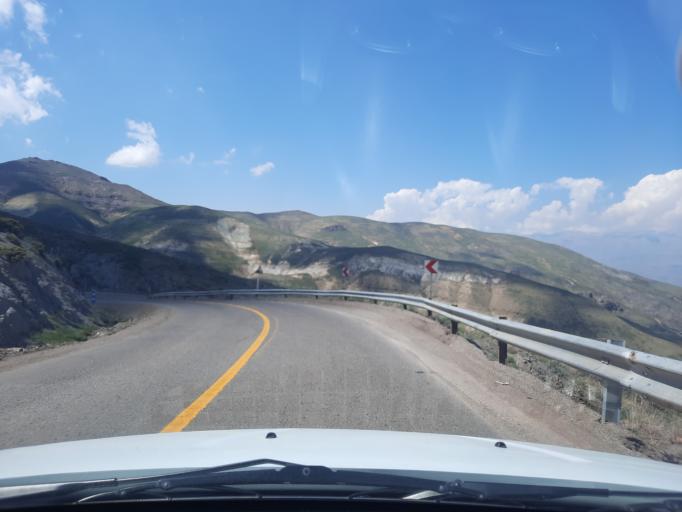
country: IR
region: Qazvin
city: Qazvin
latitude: 36.3972
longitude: 50.2151
